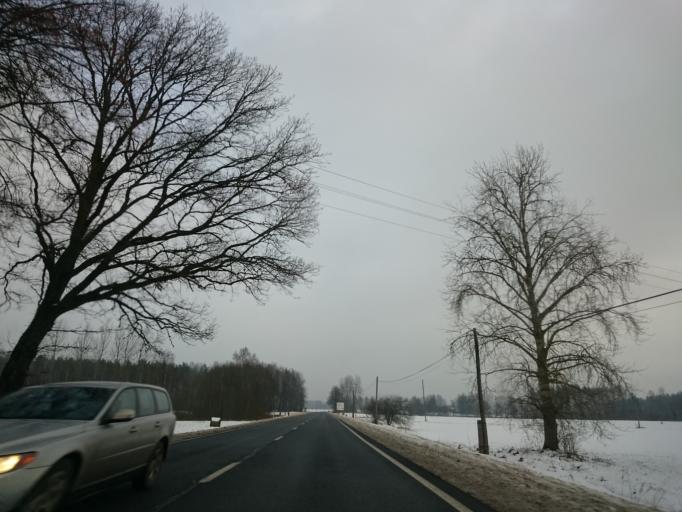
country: LV
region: Pargaujas
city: Stalbe
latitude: 57.3360
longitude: 24.9282
